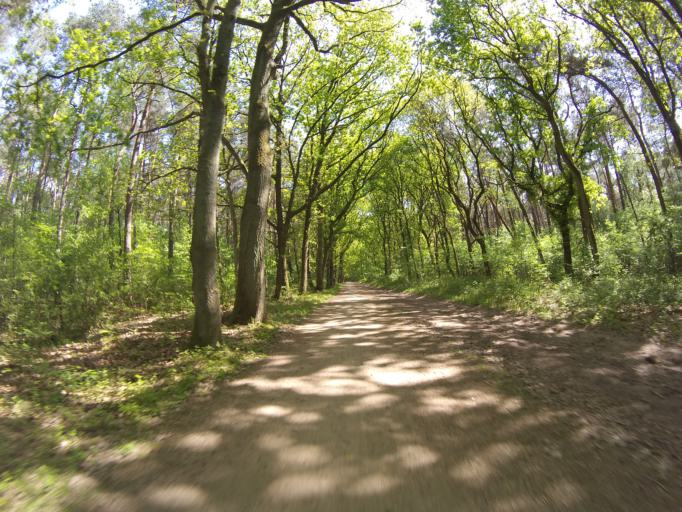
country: NL
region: North Holland
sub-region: Gemeente Hilversum
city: Hilversum
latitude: 52.1936
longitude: 5.1713
